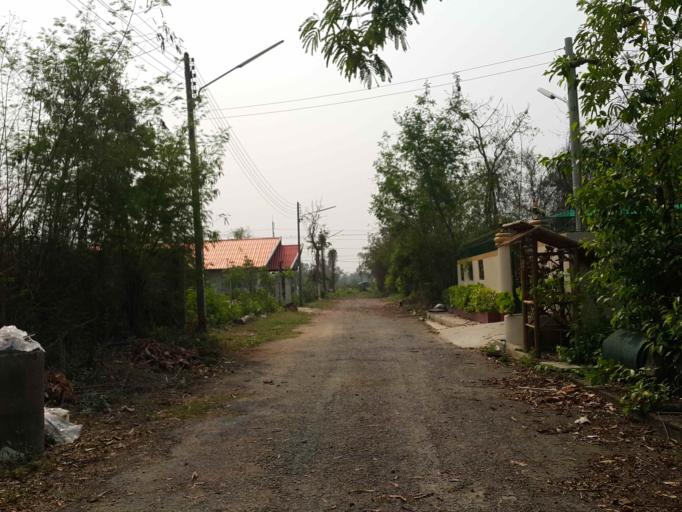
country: TH
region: Chiang Mai
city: San Kamphaeng
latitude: 18.7672
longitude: 99.0648
